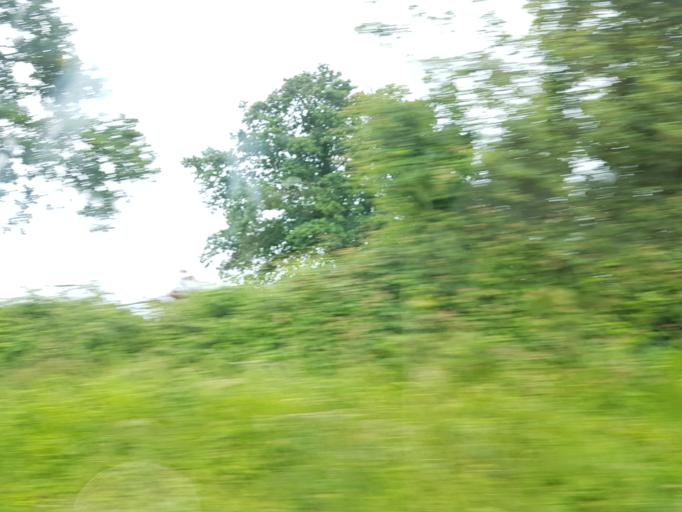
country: FR
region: Bourgogne
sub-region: Departement de la Nievre
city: Corbigny
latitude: 47.2180
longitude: 3.7047
